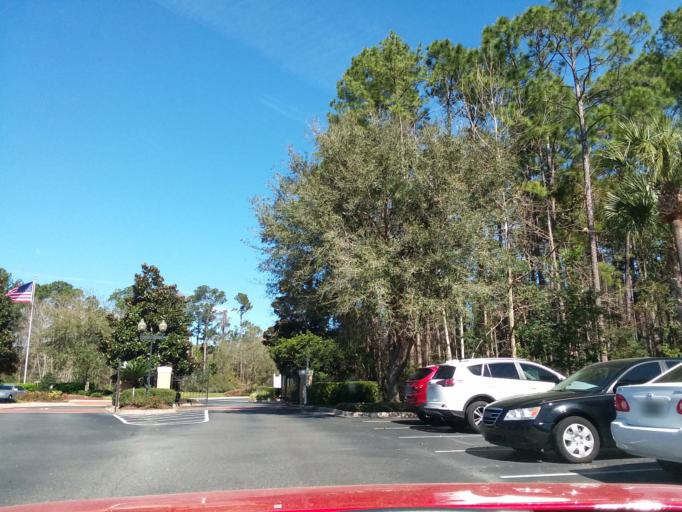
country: US
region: Florida
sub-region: Duval County
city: Atlantic Beach
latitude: 30.3190
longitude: -81.4546
